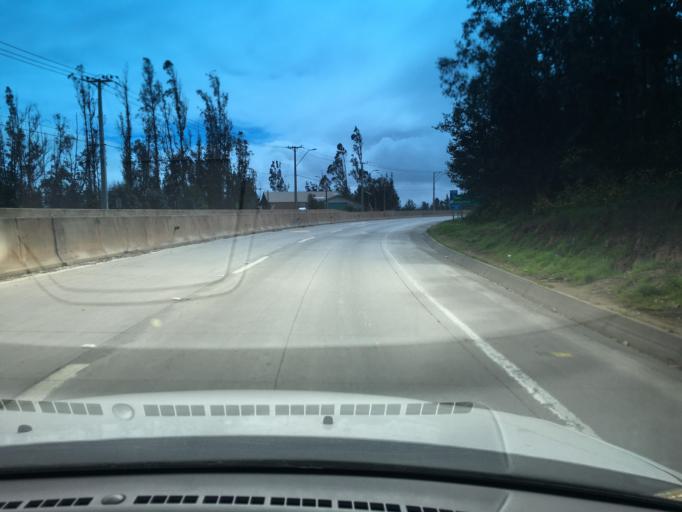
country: CL
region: Valparaiso
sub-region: Provincia de Valparaiso
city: Valparaiso
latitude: -33.0987
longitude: -71.5795
